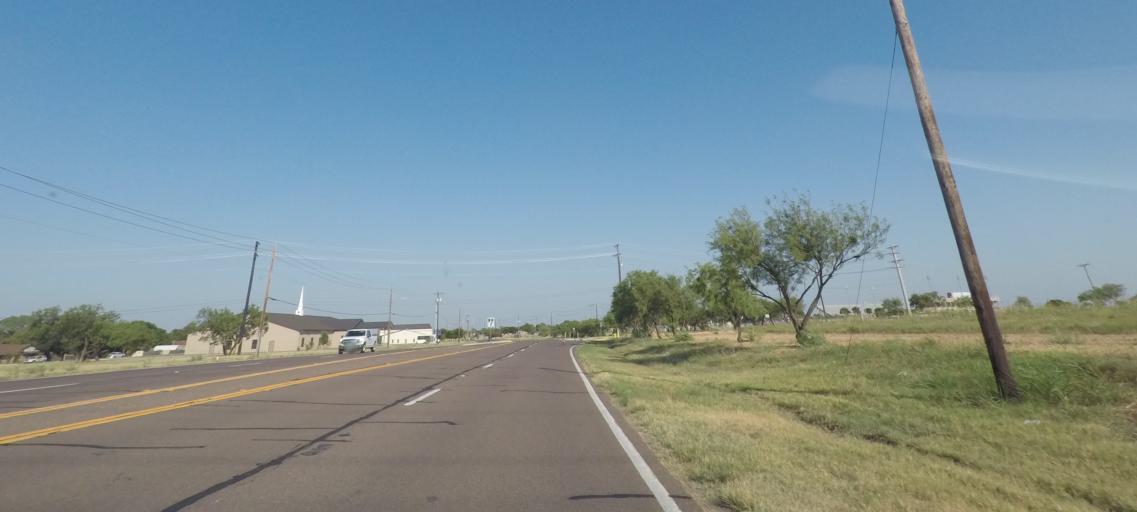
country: US
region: Texas
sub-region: Wichita County
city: Wichita Falls
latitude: 33.8589
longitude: -98.5874
